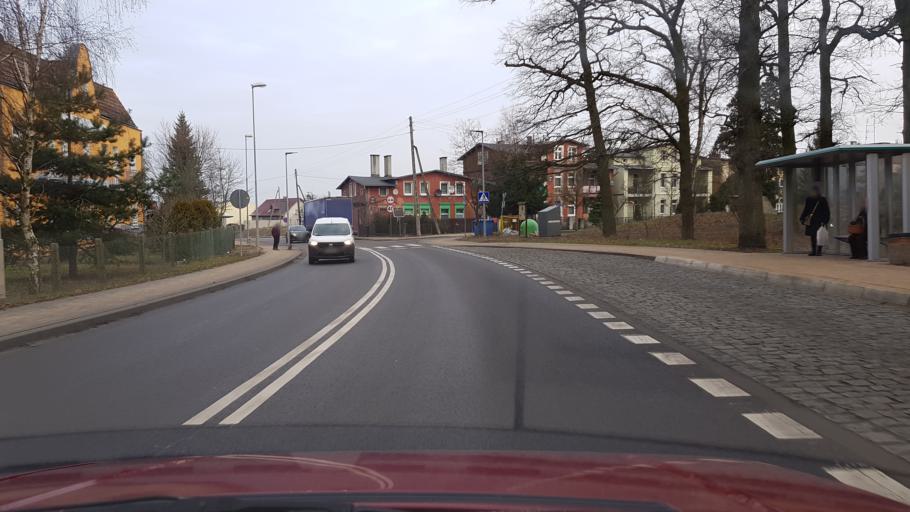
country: PL
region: West Pomeranian Voivodeship
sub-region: Powiat policki
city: Police
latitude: 53.5360
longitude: 14.5786
